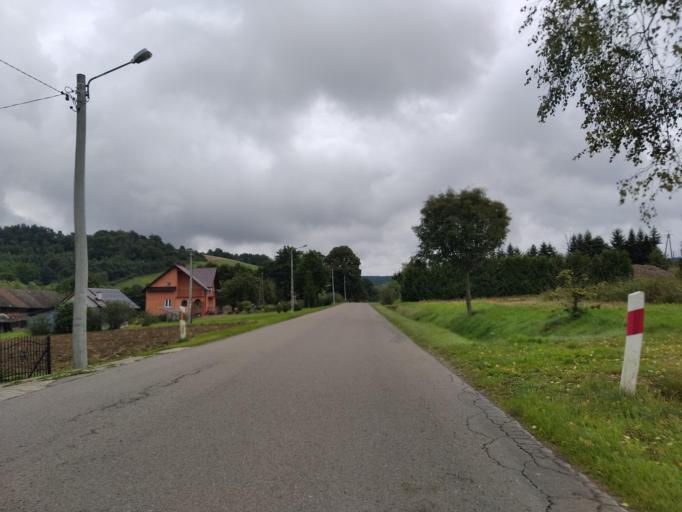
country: PL
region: Subcarpathian Voivodeship
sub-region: Powiat brzozowski
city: Nozdrzec
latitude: 49.7290
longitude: 22.2752
